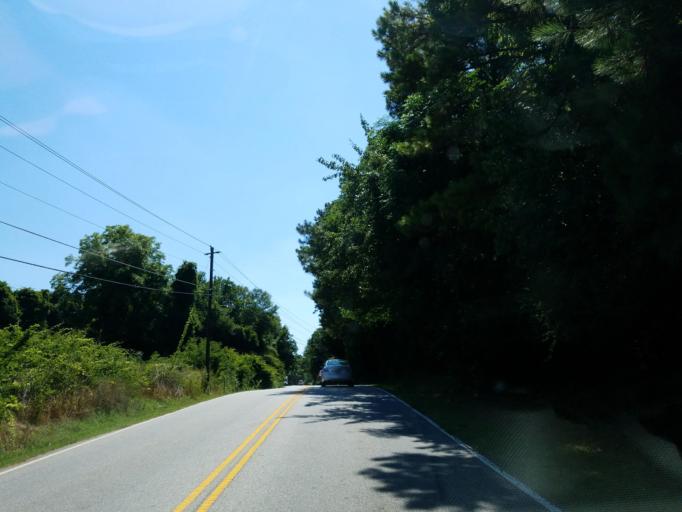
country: US
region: Georgia
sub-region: Clayton County
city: Lovejoy
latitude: 33.4492
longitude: -84.3186
